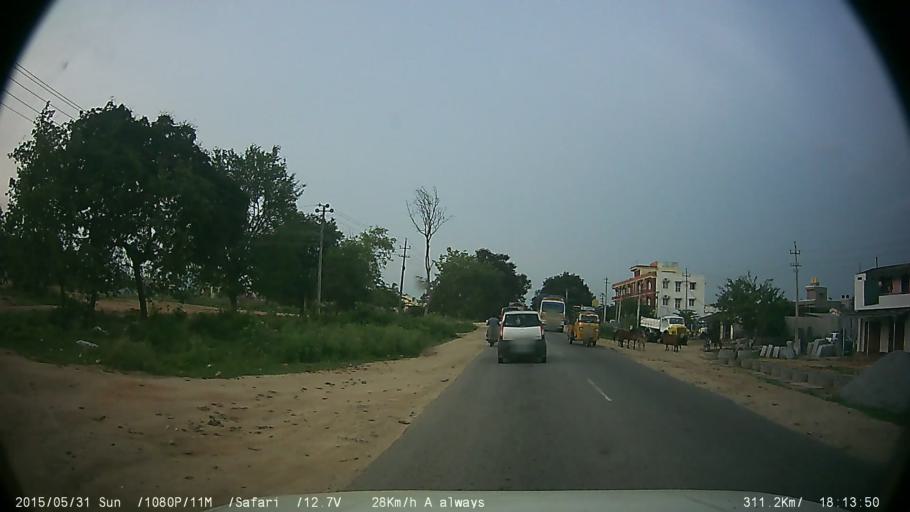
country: IN
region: Karnataka
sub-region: Mysore
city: Nanjangud
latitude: 12.1043
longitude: 76.6718
